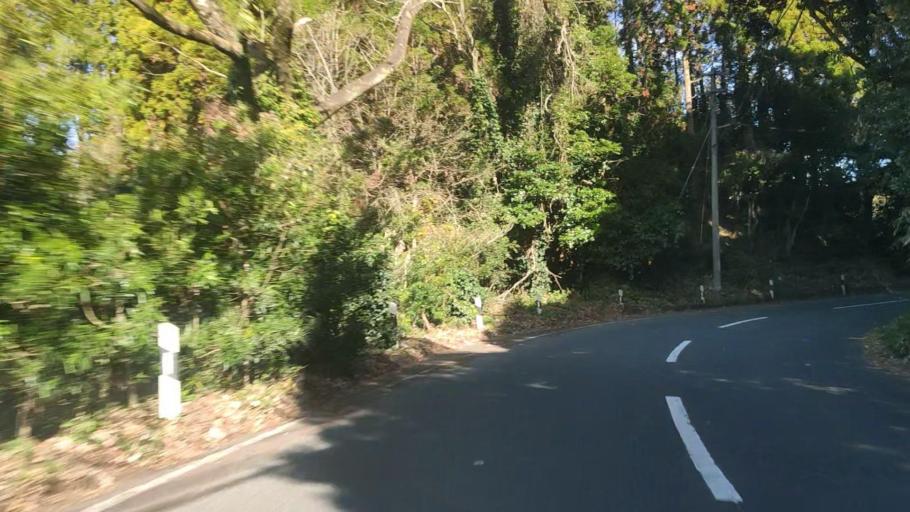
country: JP
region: Kagoshima
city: Kokubu-matsuki
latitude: 31.6676
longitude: 130.8255
